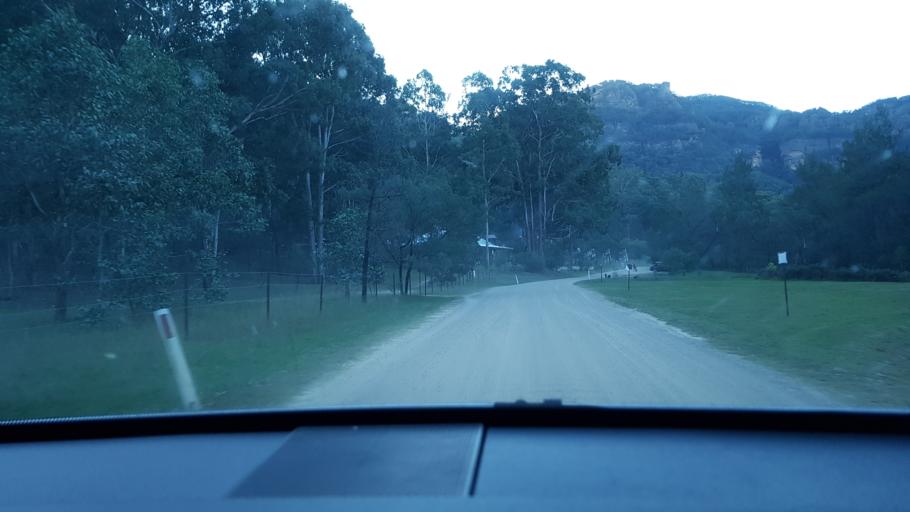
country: AU
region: New South Wales
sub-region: Lithgow
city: Portland
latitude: -33.1806
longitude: 150.2363
